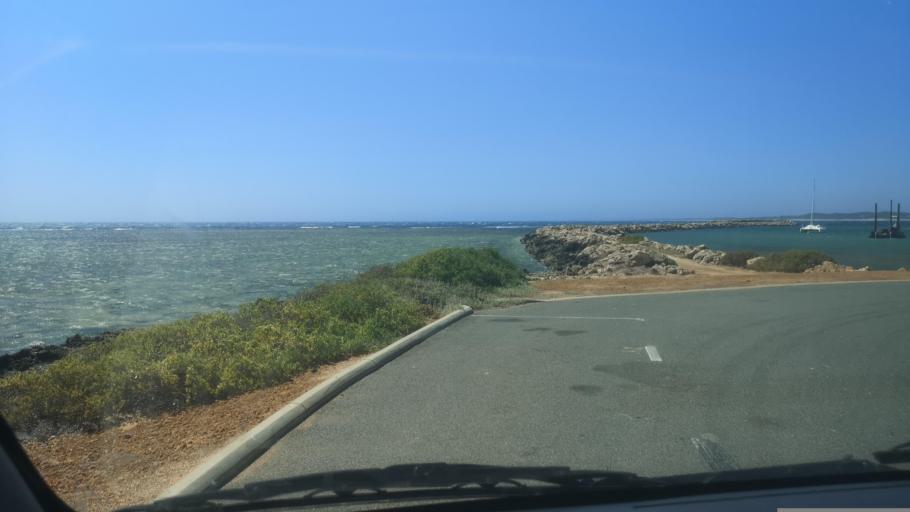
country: AU
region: Western Australia
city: Port Denison
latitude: -29.2769
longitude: 114.9146
